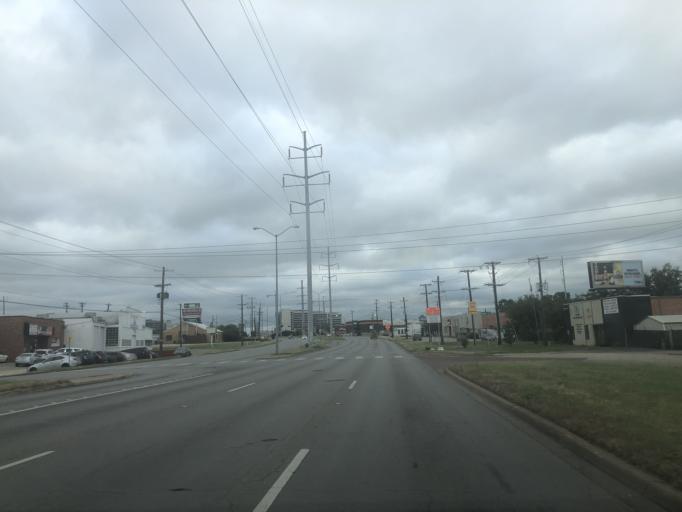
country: US
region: Texas
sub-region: Dallas County
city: University Park
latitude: 32.8284
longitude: -96.8571
